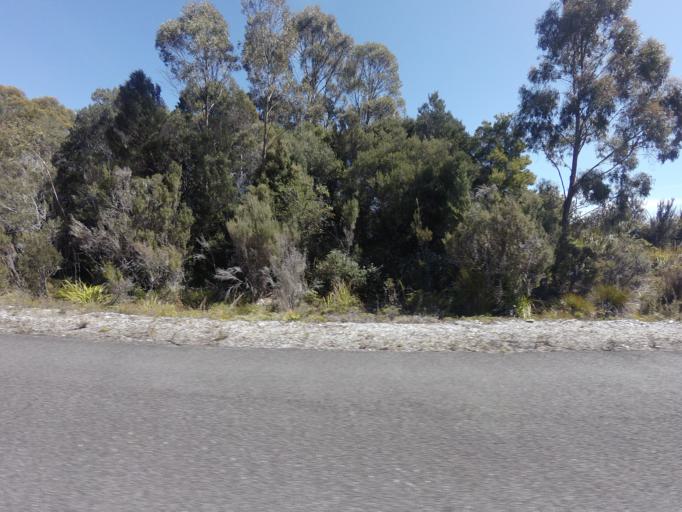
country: AU
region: Tasmania
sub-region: Huon Valley
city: Geeveston
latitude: -42.8418
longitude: 146.1634
